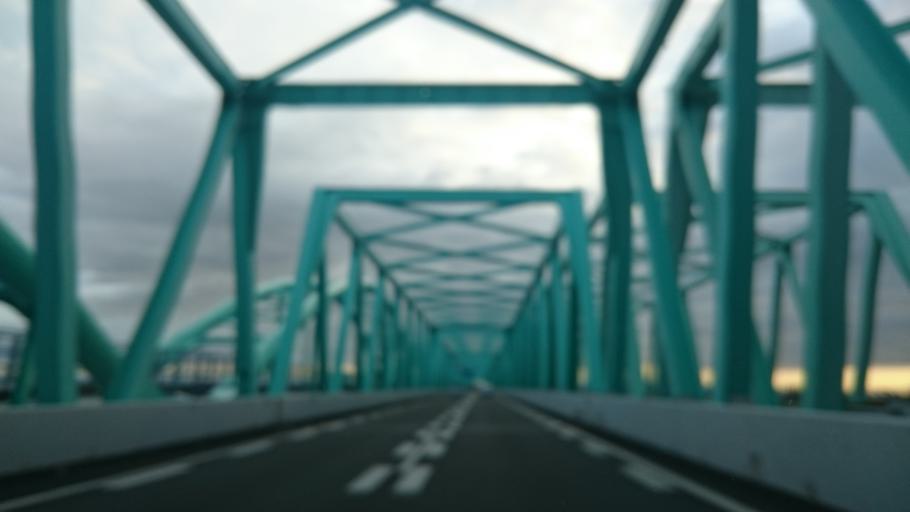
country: JP
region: Aichi
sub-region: Tsushima-shi
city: Tsushima
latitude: 35.1151
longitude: 136.7023
